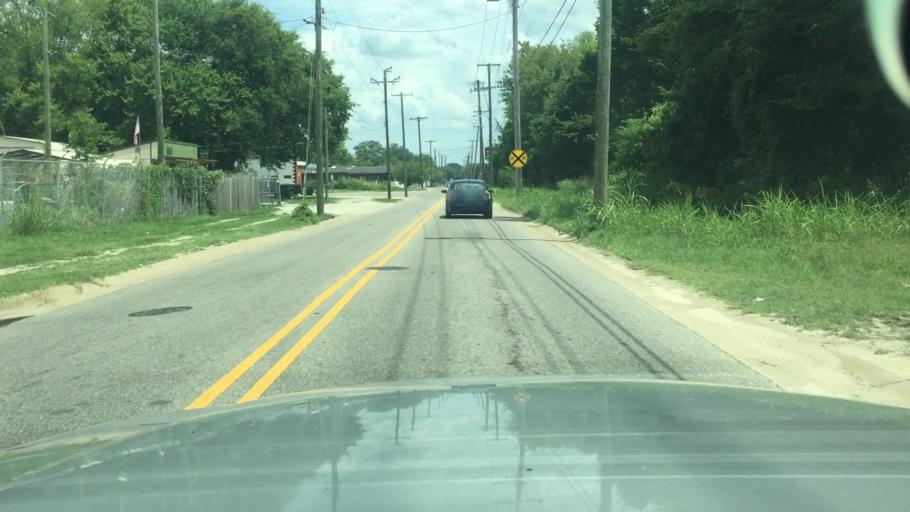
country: US
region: North Carolina
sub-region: Cumberland County
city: Fayetteville
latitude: 35.0480
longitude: -78.8876
